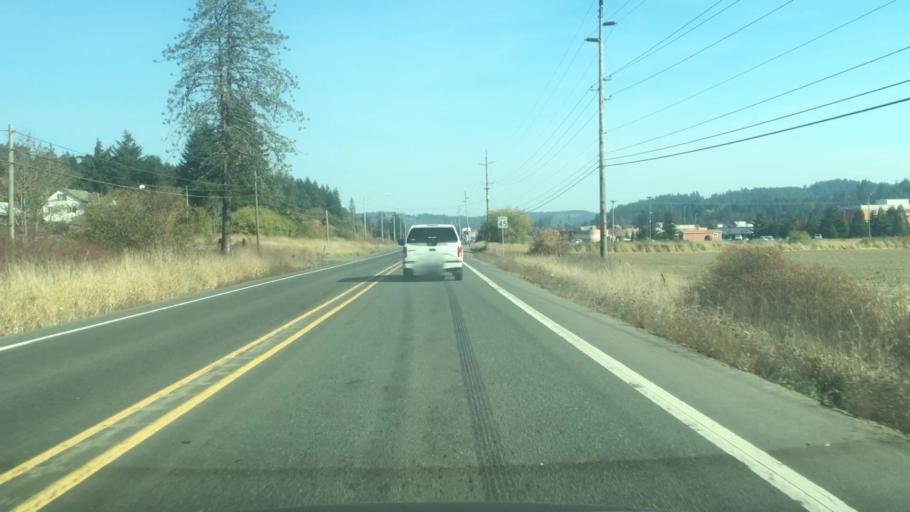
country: US
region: Oregon
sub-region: Polk County
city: Grand Ronde
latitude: 45.0593
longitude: -123.5891
